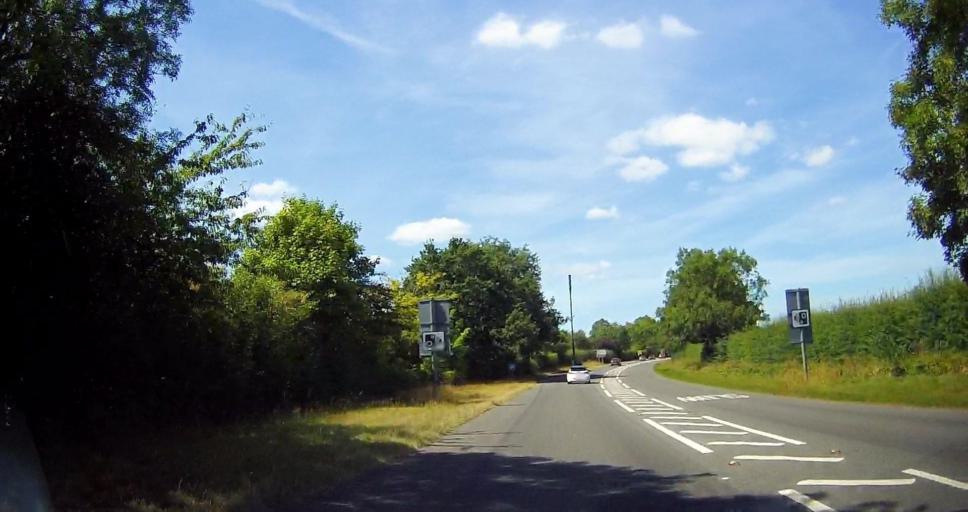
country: GB
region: England
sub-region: Shropshire
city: Albrighton
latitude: 52.6438
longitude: -2.2856
